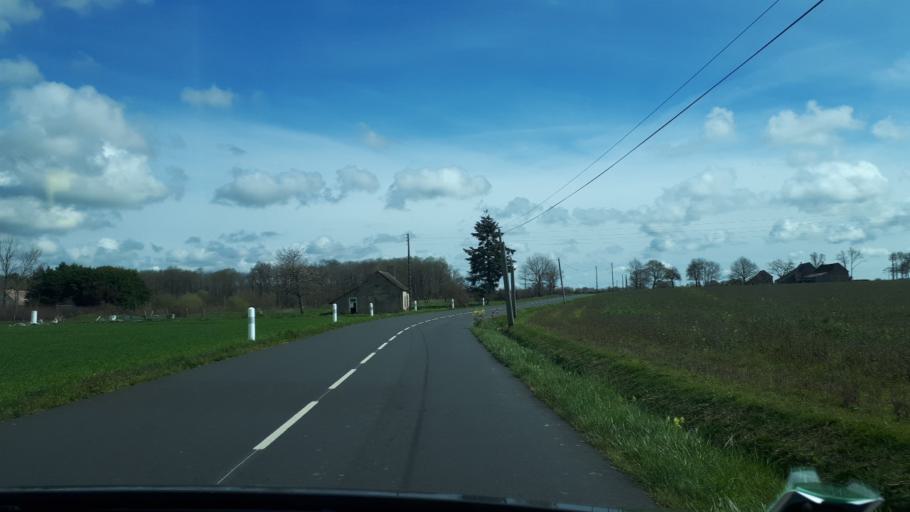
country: FR
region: Pays de la Loire
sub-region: Departement de la Sarthe
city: Bouloire
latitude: 47.8929
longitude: 0.5482
